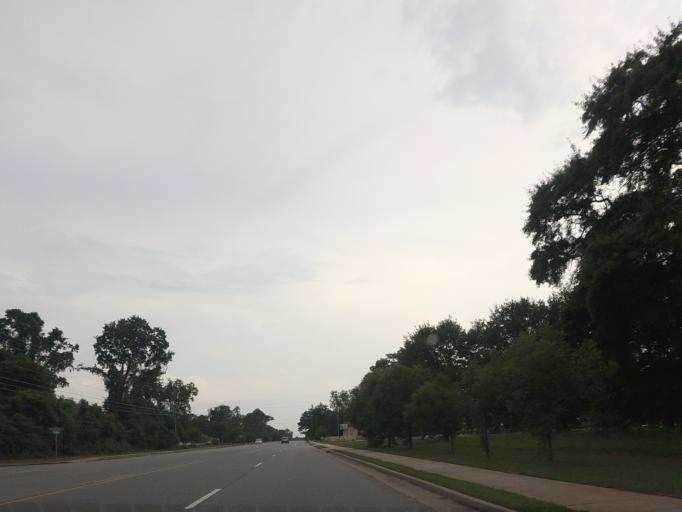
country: US
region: Georgia
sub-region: Bibb County
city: Macon
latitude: 32.7398
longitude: -83.6760
